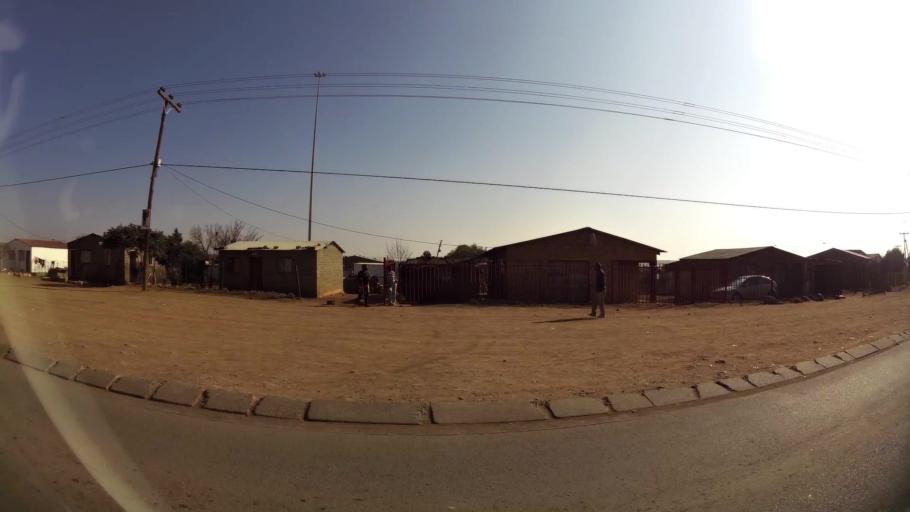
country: ZA
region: Orange Free State
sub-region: Mangaung Metropolitan Municipality
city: Bloemfontein
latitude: -29.1753
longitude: 26.2277
